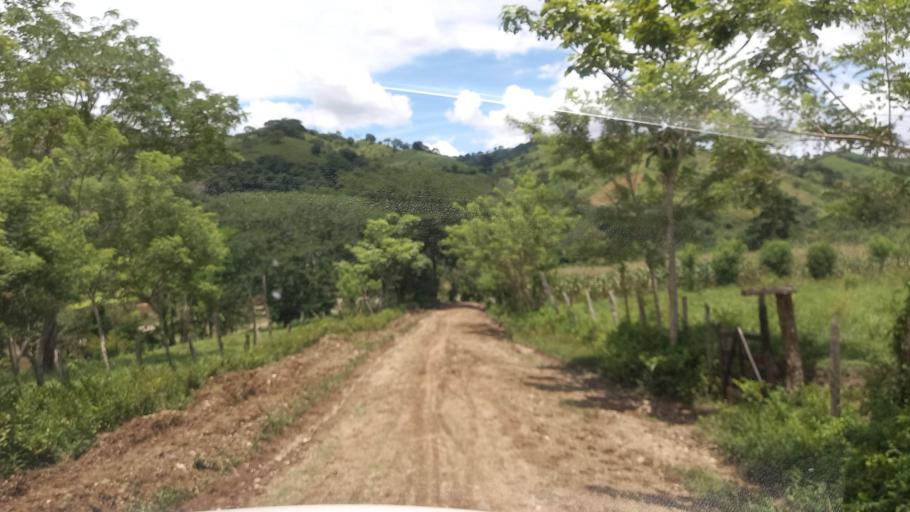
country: NI
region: Nueva Segovia
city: Wiwili
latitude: 13.7411
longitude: -85.7892
